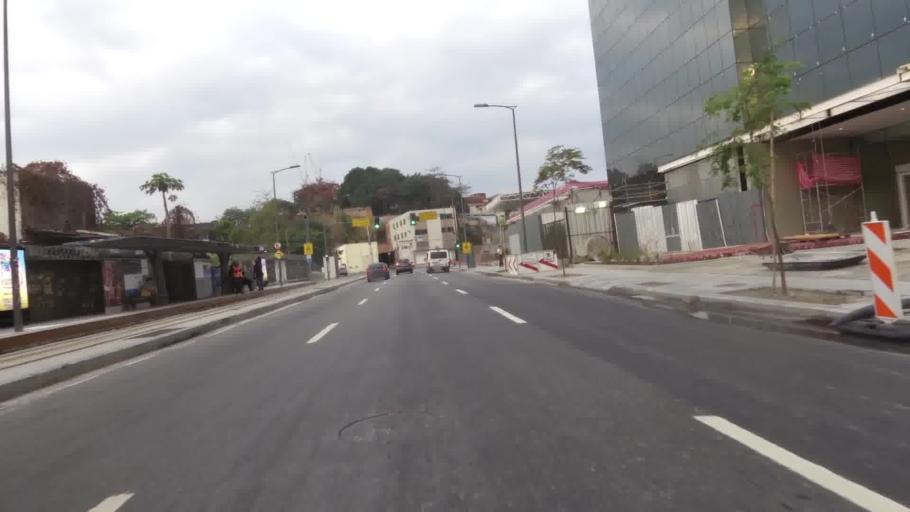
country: BR
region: Rio de Janeiro
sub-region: Rio De Janeiro
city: Rio de Janeiro
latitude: -22.8969
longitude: -43.2021
